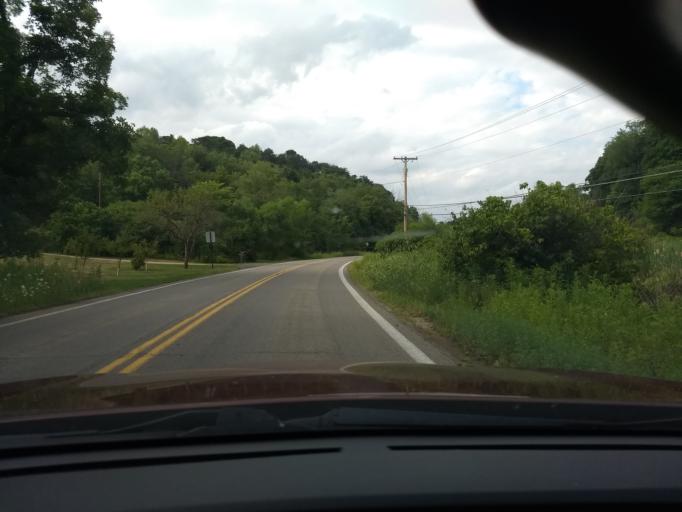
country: US
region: Pennsylvania
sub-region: Allegheny County
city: Bell Acres
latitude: 40.6281
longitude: -80.1426
